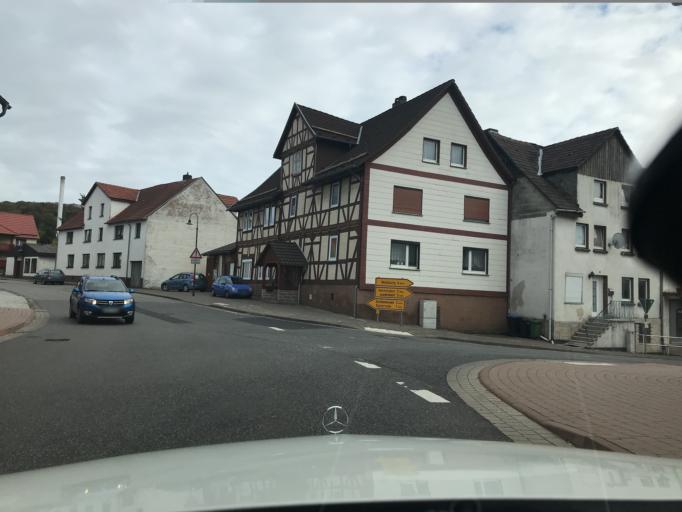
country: DE
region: Hesse
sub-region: Regierungsbezirk Kassel
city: Grossalmerode
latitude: 51.2320
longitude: 9.7688
